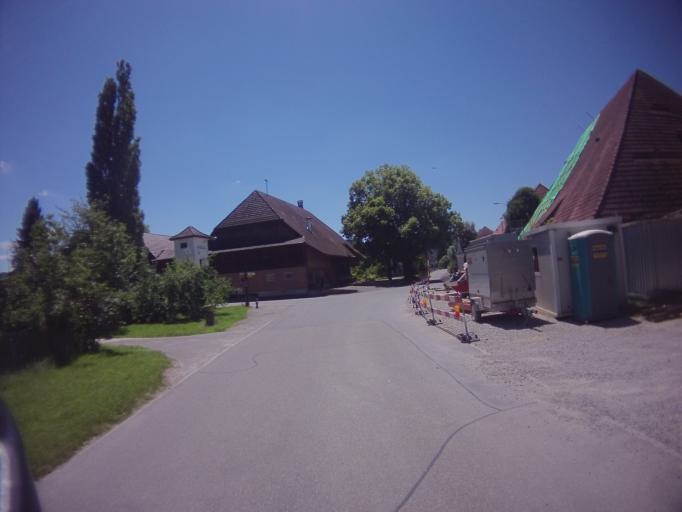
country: CH
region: Bern
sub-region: Bern-Mittelland District
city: Urtenen
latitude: 47.0304
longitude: 7.5137
